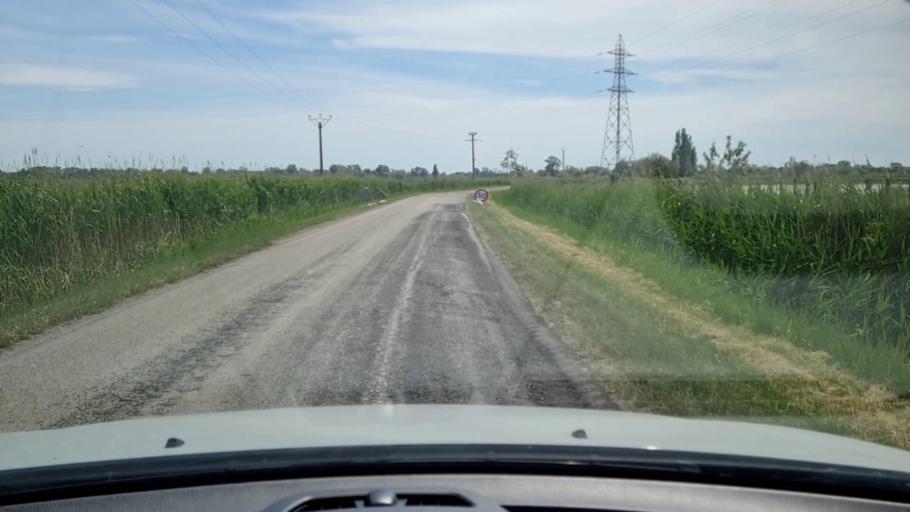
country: FR
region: Languedoc-Roussillon
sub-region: Departement du Gard
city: Saint-Gilles
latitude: 43.5735
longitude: 4.3973
